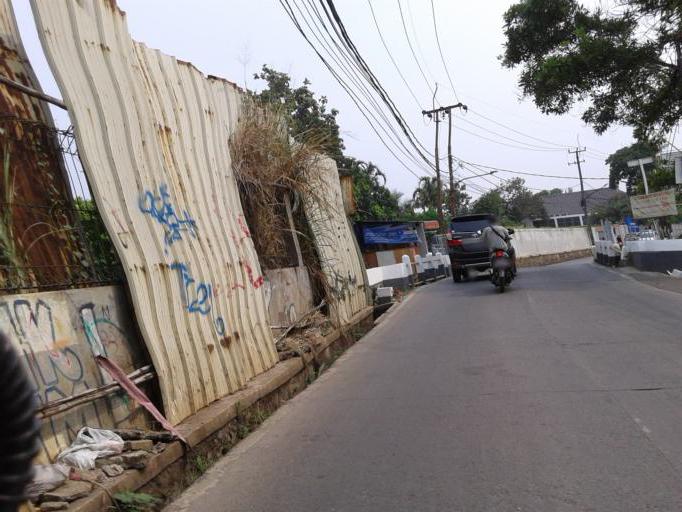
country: ID
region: Banten
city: South Tangerang
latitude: -6.2930
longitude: 106.7360
